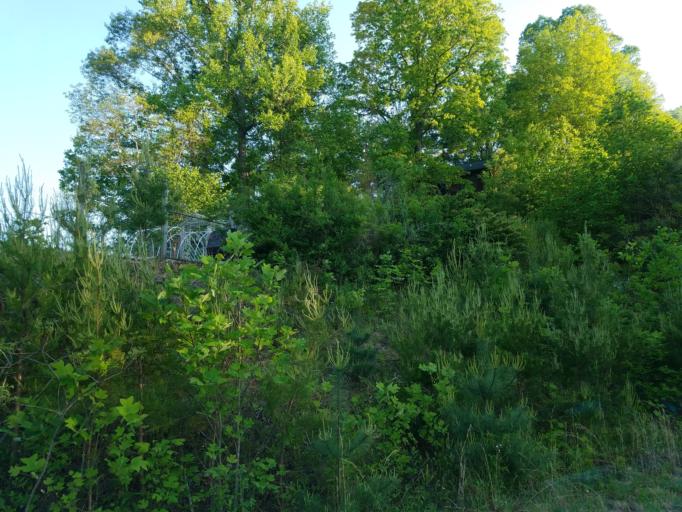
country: US
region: Georgia
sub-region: Union County
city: Blairsville
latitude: 34.7178
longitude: -84.0608
